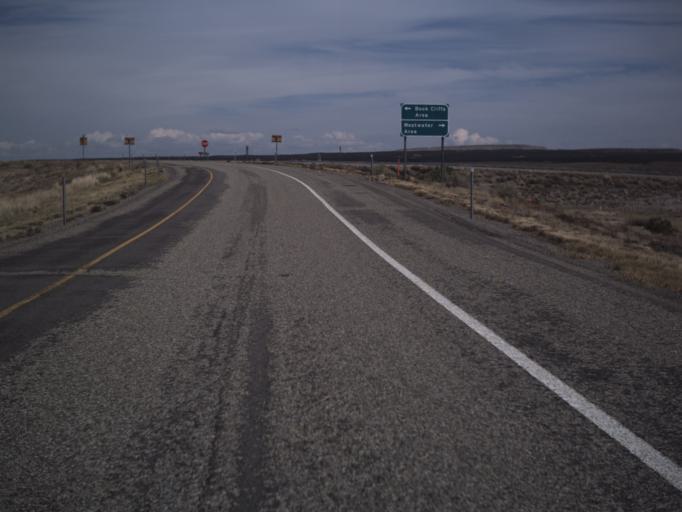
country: US
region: Colorado
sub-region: Mesa County
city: Loma
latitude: 39.1119
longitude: -109.1855
